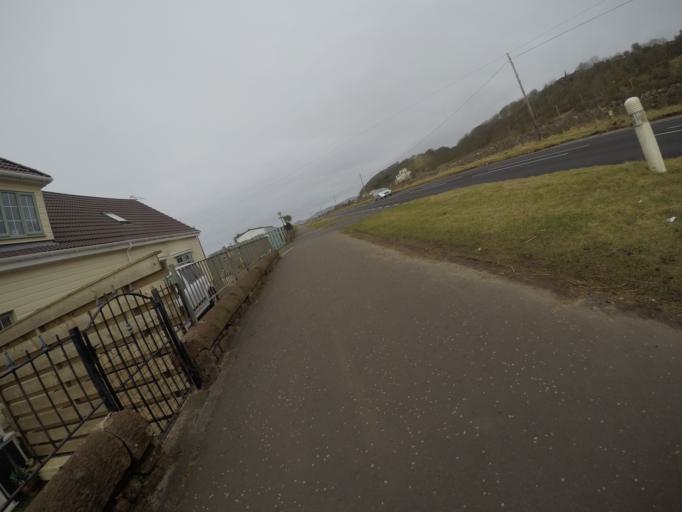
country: GB
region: Scotland
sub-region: North Ayrshire
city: West Kilbride
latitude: 55.6650
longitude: -4.8374
